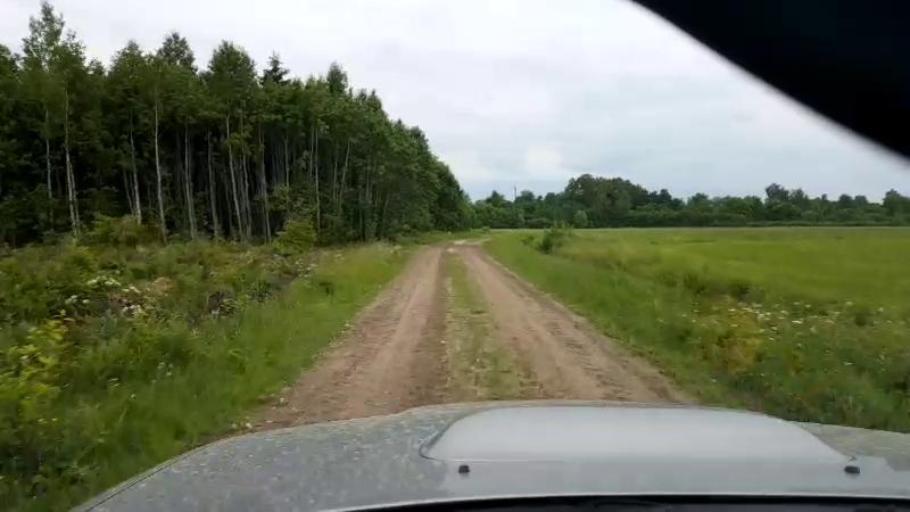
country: EE
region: Paernumaa
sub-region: Tootsi vald
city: Tootsi
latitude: 58.5970
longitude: 24.6628
